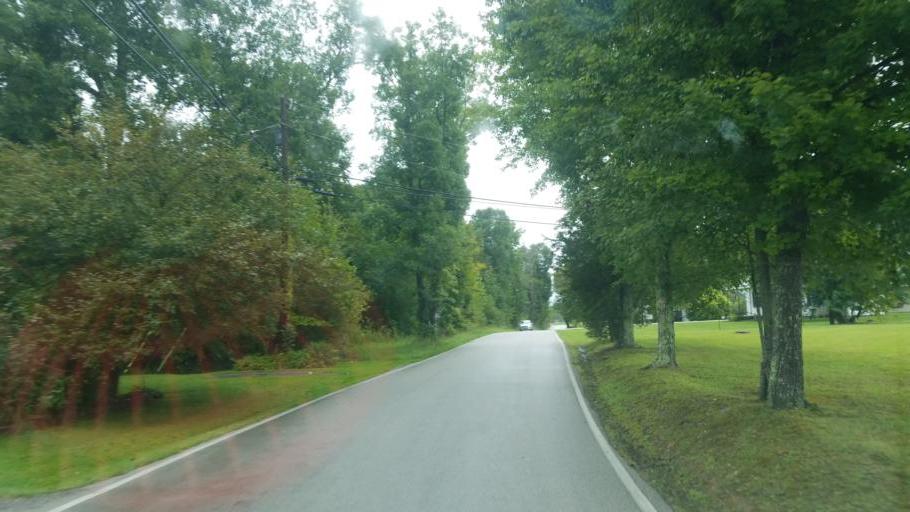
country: US
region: Kentucky
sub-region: Rowan County
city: Morehead
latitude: 38.1553
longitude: -83.5085
